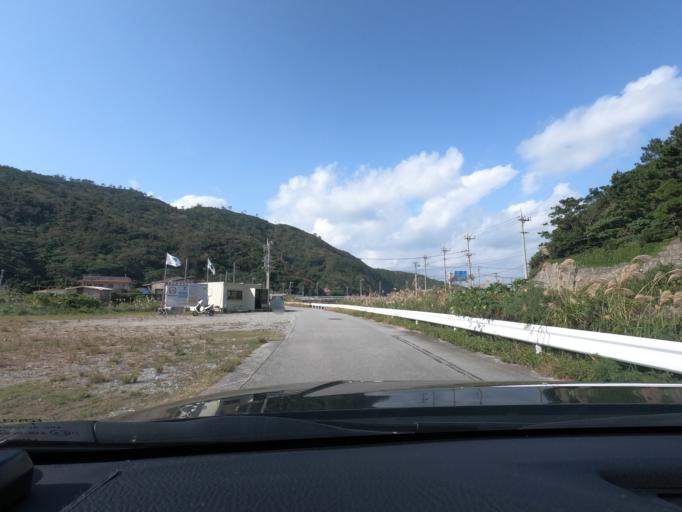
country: JP
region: Okinawa
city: Nago
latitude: 26.7663
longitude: 128.2060
